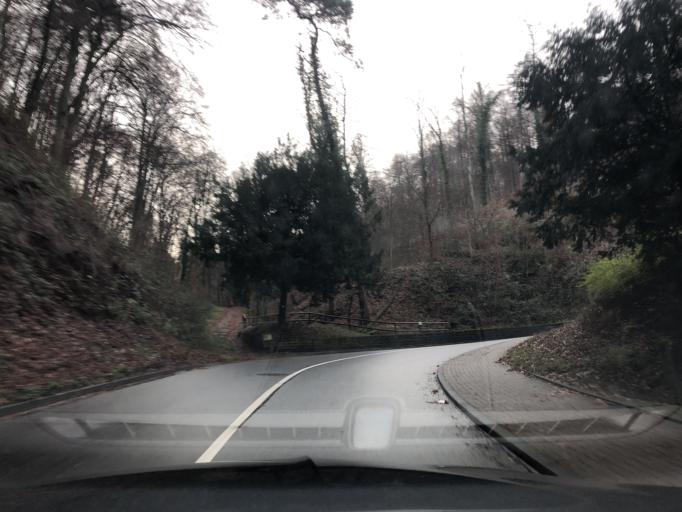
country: DE
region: Baden-Wuerttemberg
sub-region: Karlsruhe Region
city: Heidelberg
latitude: 49.3965
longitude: 8.6987
